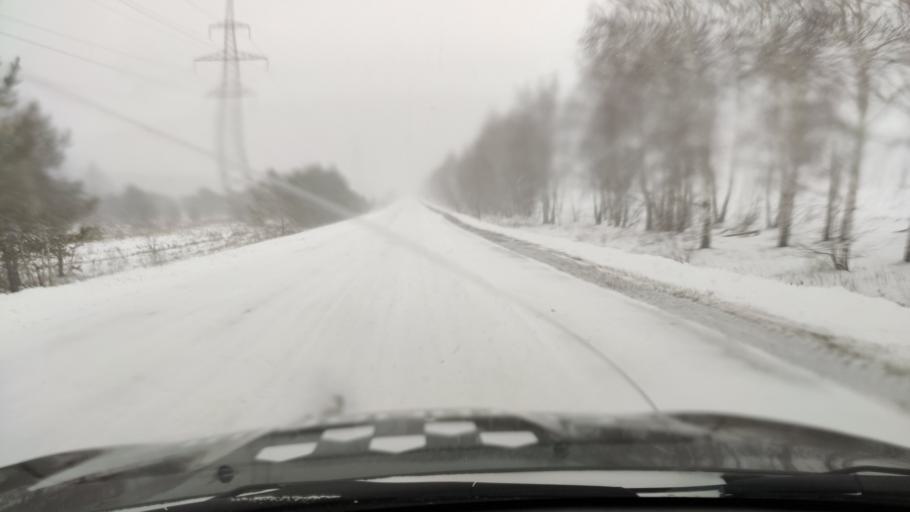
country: RU
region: Samara
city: Povolzhskiy
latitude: 53.5278
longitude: 49.7146
